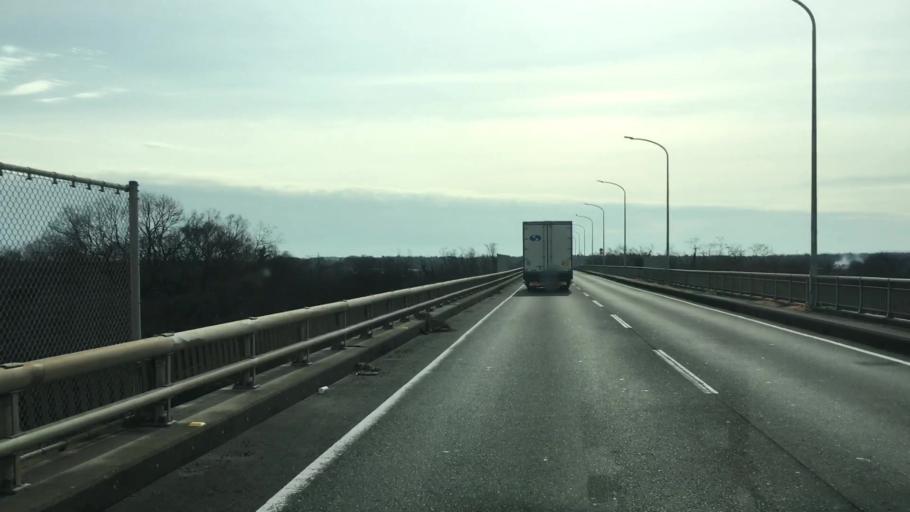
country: JP
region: Saitama
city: Kumagaya
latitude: 36.1408
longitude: 139.3232
